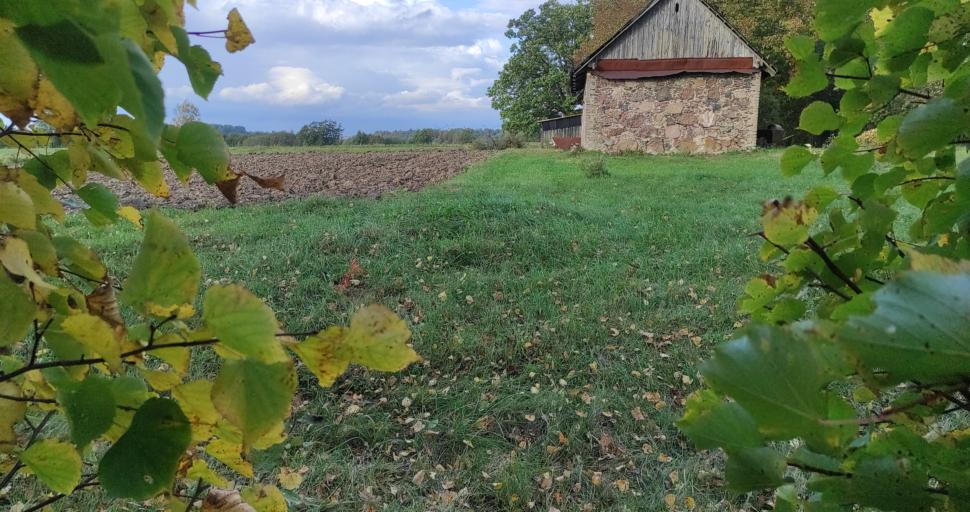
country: LV
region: Talsu Rajons
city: Sabile
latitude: 56.9026
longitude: 22.4213
